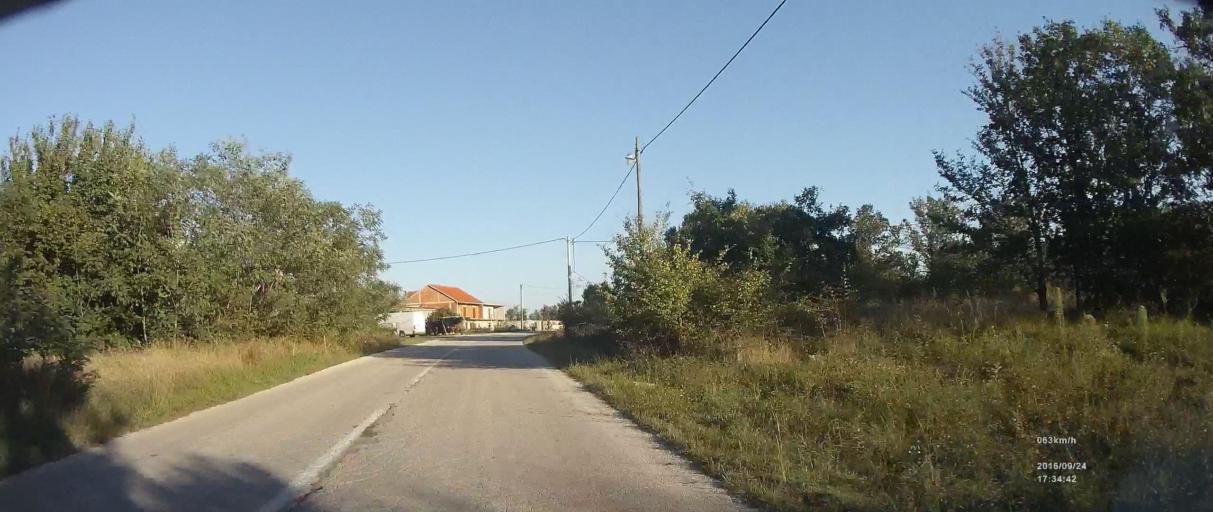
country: HR
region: Zadarska
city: Posedarje
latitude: 44.1657
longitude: 15.4625
